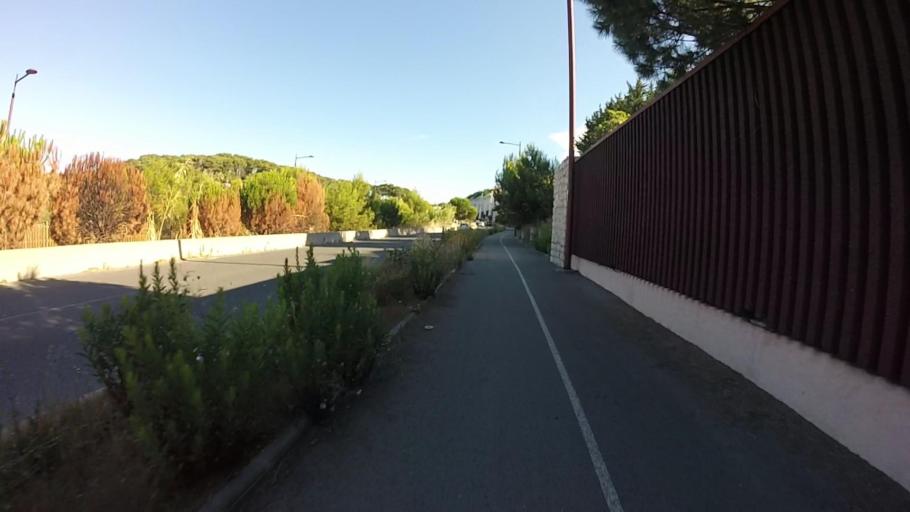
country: FR
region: Provence-Alpes-Cote d'Azur
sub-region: Departement des Alpes-Maritimes
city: Biot
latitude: 43.5904
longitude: 7.0924
